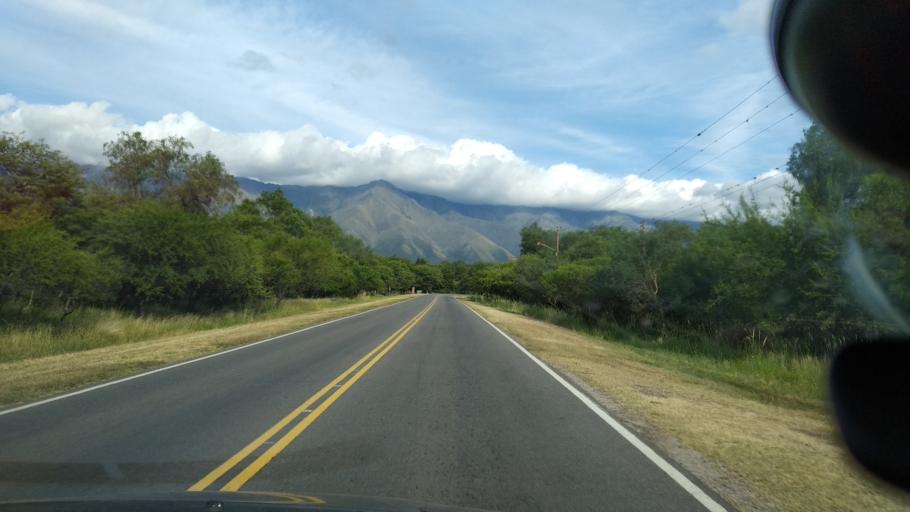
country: AR
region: Cordoba
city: Villa Las Rosas
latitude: -32.0101
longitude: -65.0509
